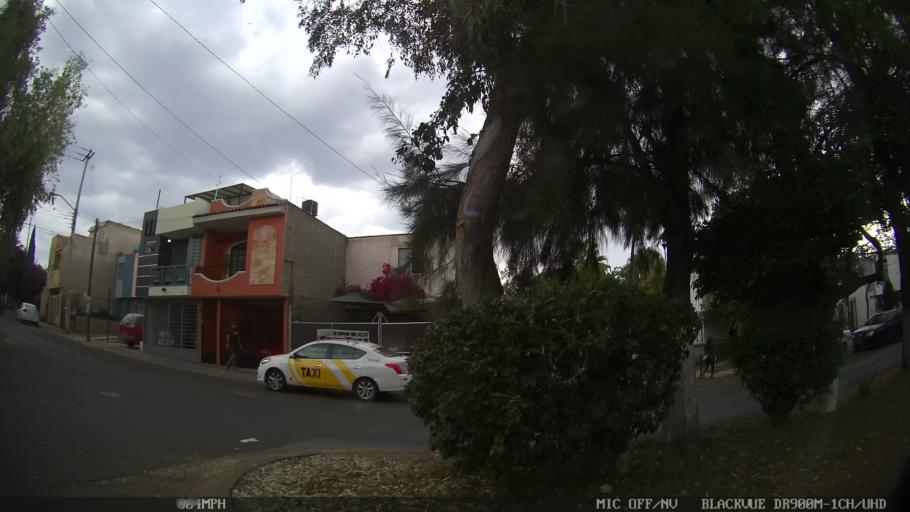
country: MX
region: Jalisco
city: Tlaquepaque
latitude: 20.6266
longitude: -103.2777
